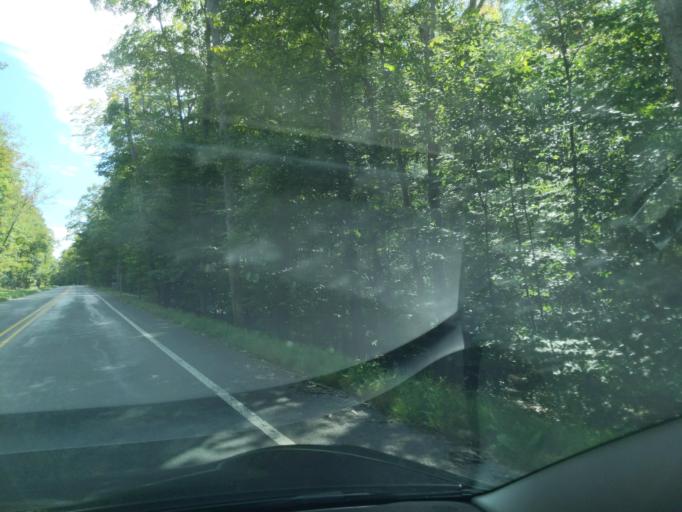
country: US
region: Michigan
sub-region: Antrim County
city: Bellaire
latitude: 45.0033
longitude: -85.2930
